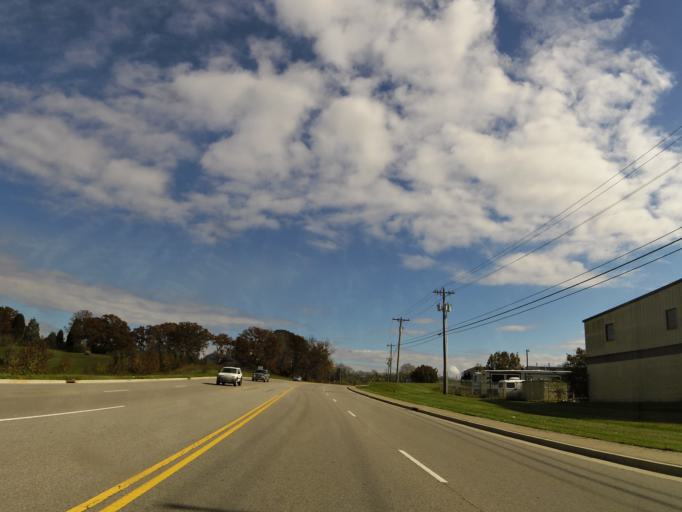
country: US
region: Tennessee
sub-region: Blount County
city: Maryville
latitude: 35.7688
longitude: -83.9997
